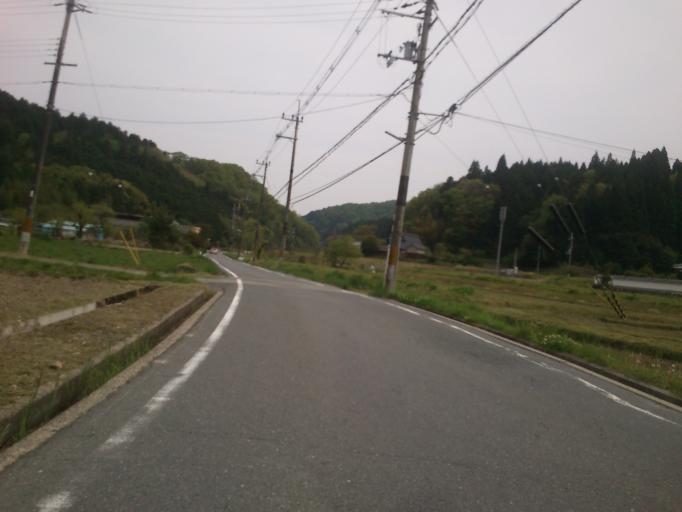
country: JP
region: Kyoto
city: Kameoka
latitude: 34.9585
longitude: 135.5332
